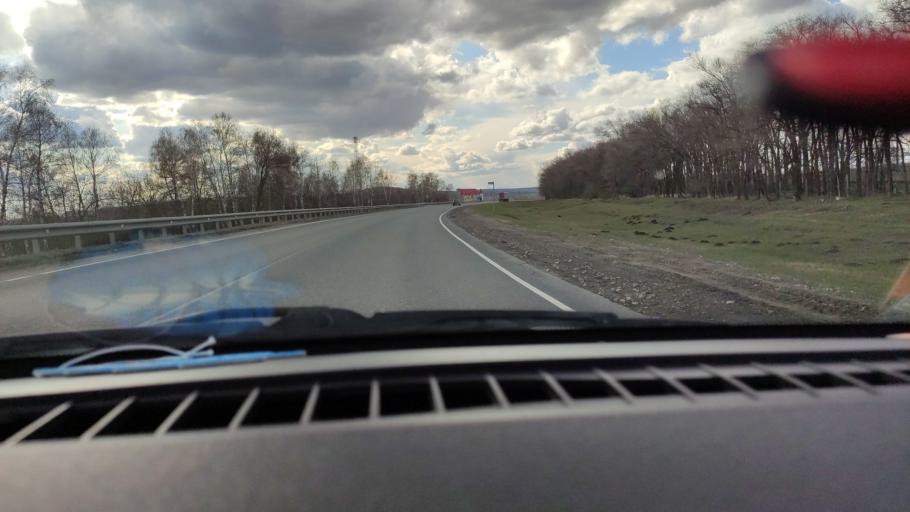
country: RU
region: Saratov
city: Tersa
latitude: 52.0838
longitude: 47.5552
